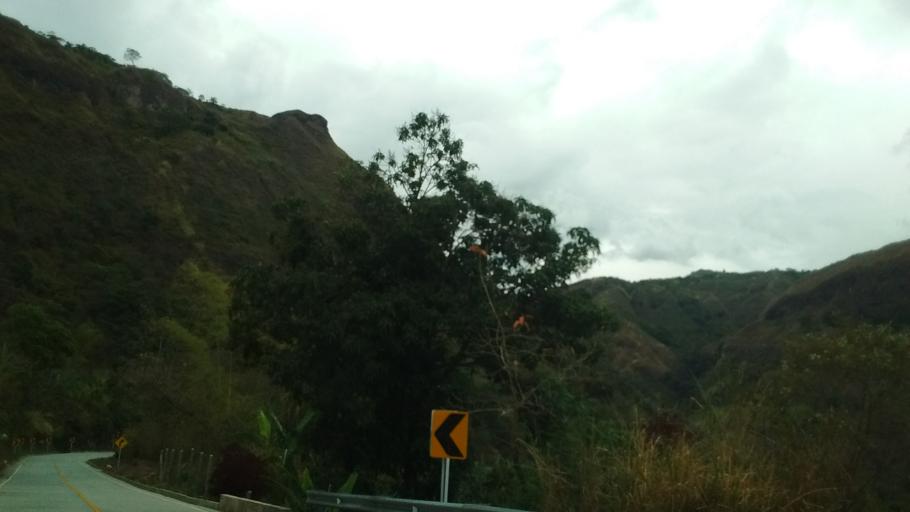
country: CO
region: Cauca
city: La Sierra
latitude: 2.1533
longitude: -76.7672
